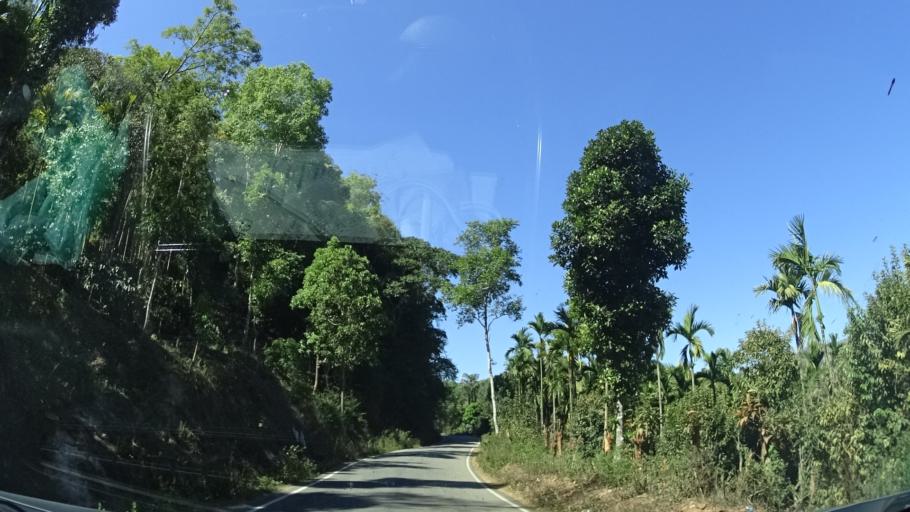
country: IN
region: Karnataka
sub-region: Chikmagalur
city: Sringeri
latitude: 13.2227
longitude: 75.3498
